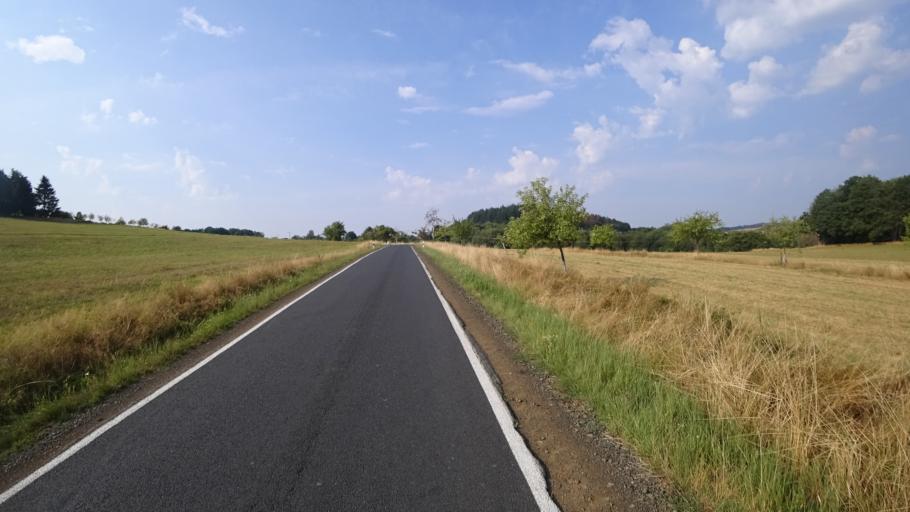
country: DE
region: Rheinland-Pfalz
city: Hilgert
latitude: 50.4633
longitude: 7.6844
